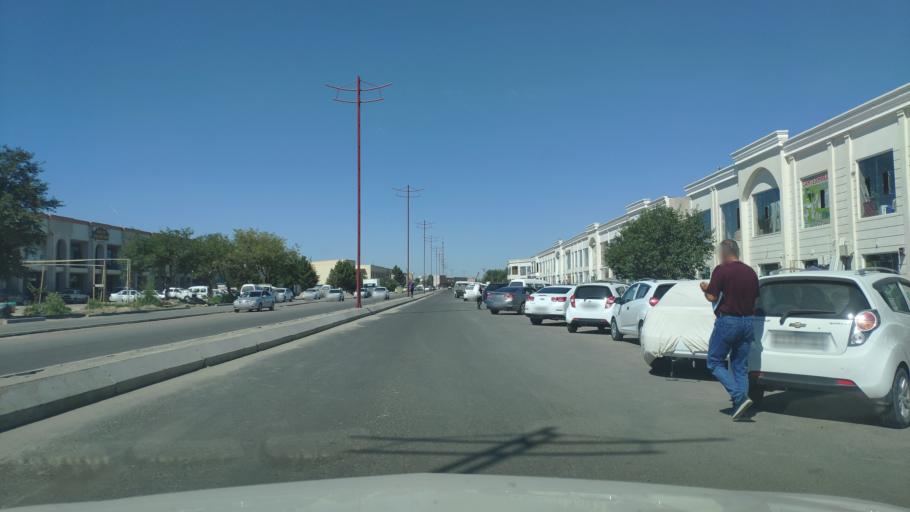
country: UZ
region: Bukhara
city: Bukhara
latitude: 39.7760
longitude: 64.3908
